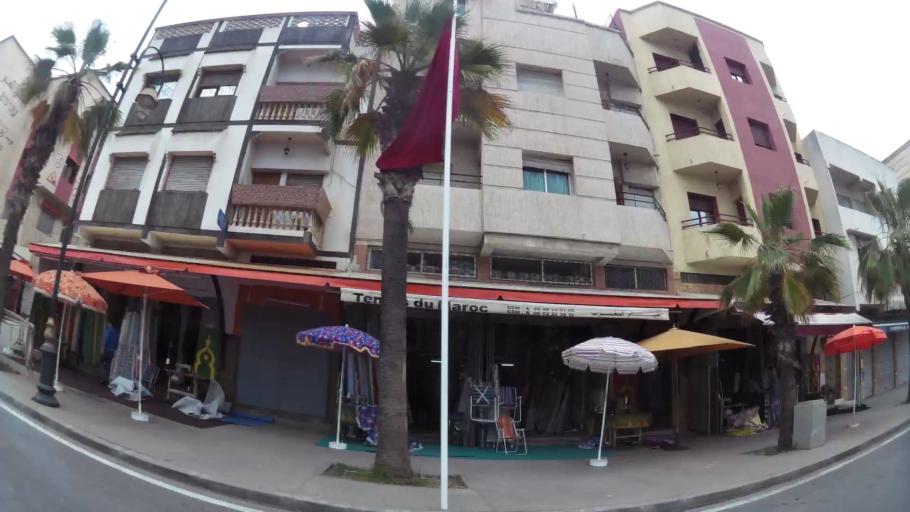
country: MA
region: Rabat-Sale-Zemmour-Zaer
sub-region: Rabat
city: Rabat
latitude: 33.9907
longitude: -6.8757
